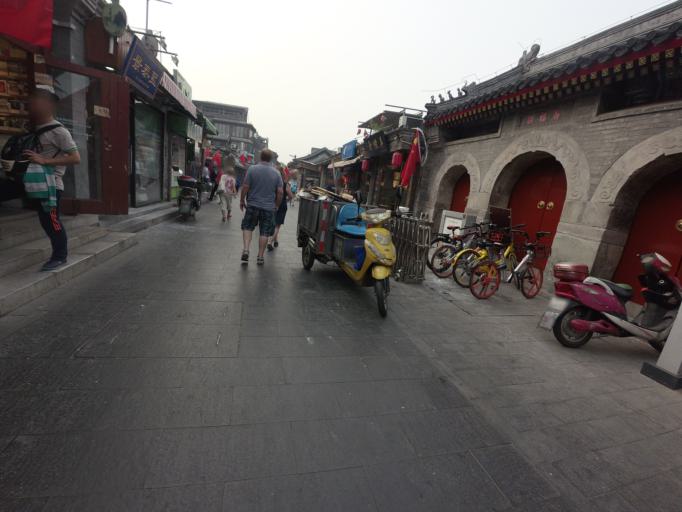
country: CN
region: Beijing
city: Jingshan
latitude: 39.9377
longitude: 116.3886
